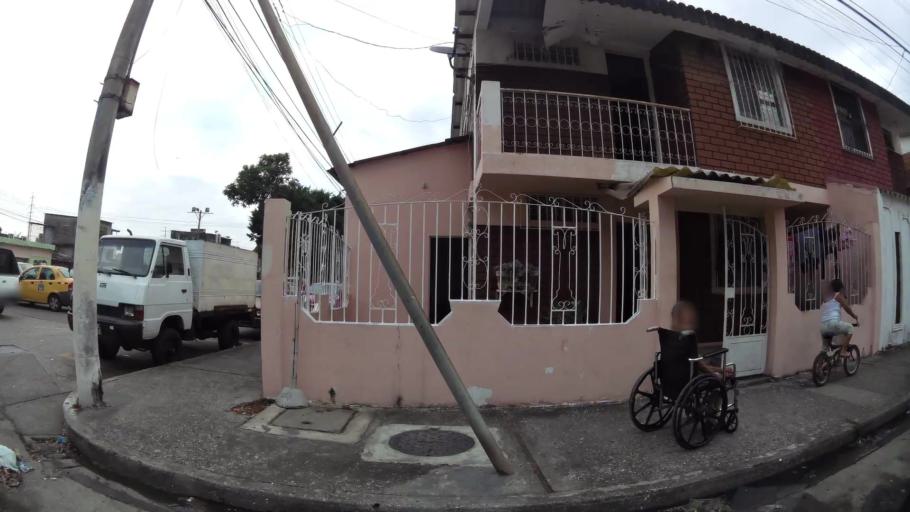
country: EC
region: Guayas
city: Guayaquil
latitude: -2.2384
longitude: -79.8900
